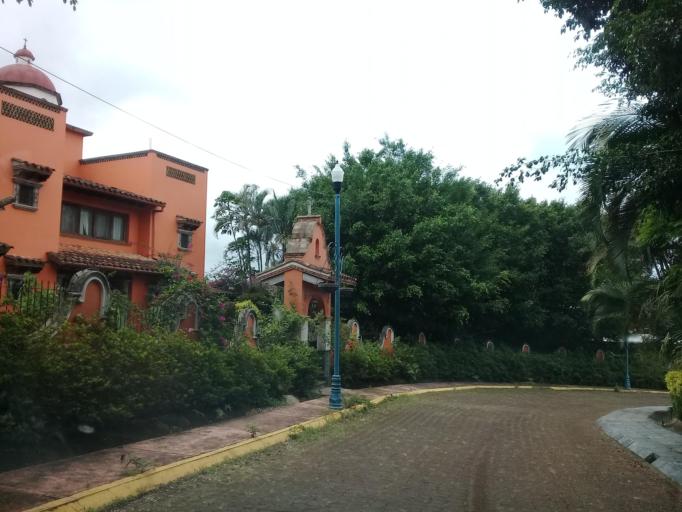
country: MX
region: Veracruz
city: El Castillo
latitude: 19.5264
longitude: -96.8759
